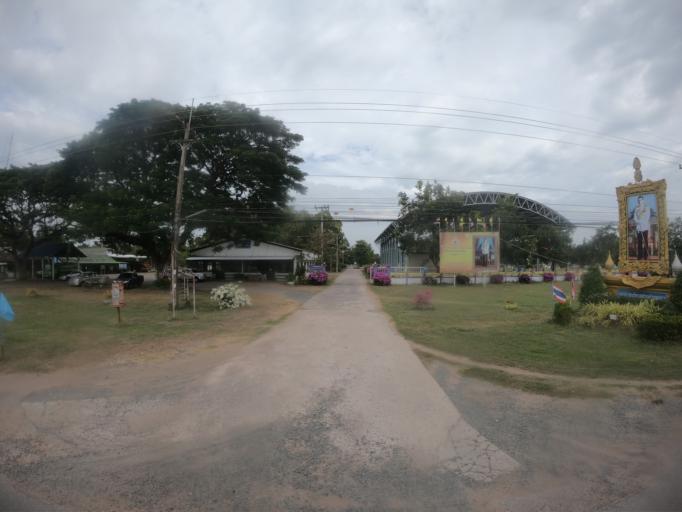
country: TH
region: Maha Sarakham
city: Maha Sarakham
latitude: 16.1463
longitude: 103.4106
